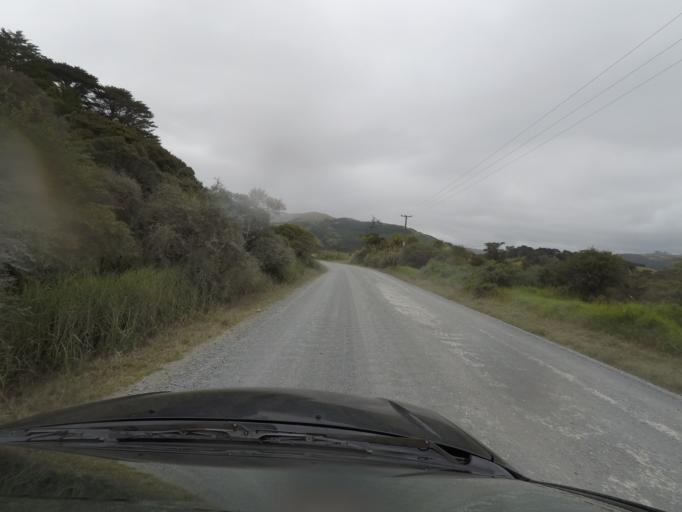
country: NZ
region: Auckland
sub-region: Auckland
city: Warkworth
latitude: -36.2530
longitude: 174.7184
